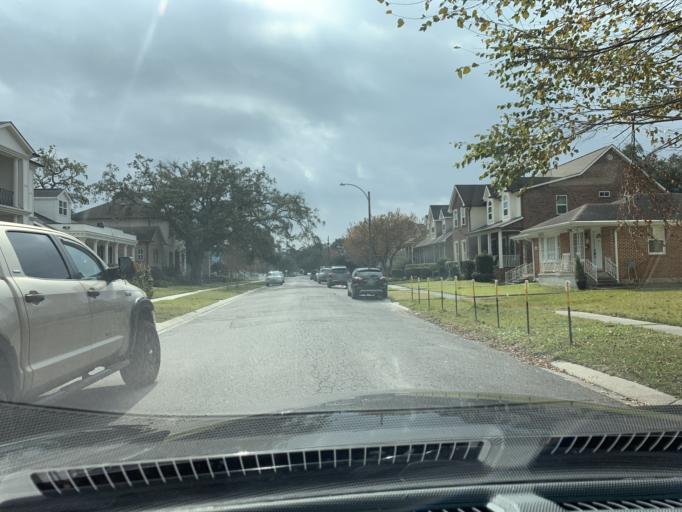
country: US
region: Louisiana
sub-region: Jefferson Parish
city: Metairie
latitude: 30.0171
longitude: -90.1033
